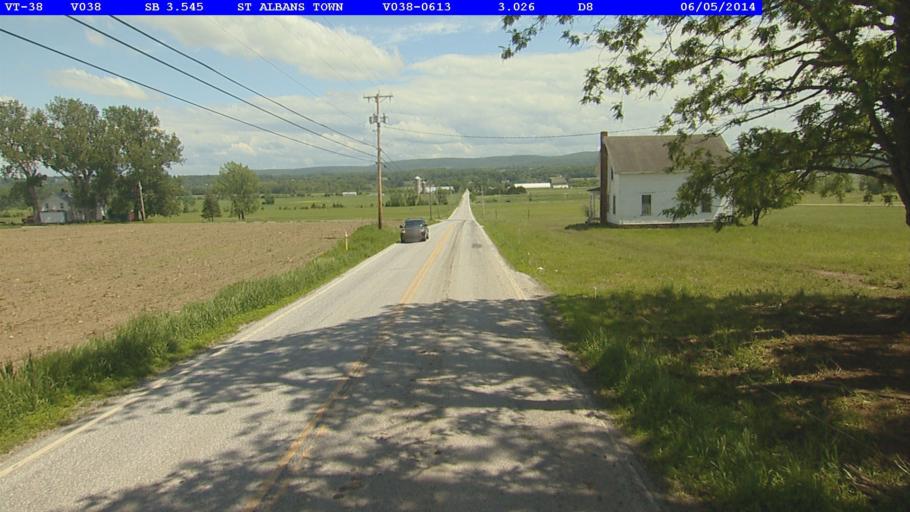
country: US
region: Vermont
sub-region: Franklin County
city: Saint Albans
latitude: 44.8534
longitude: -73.1317
